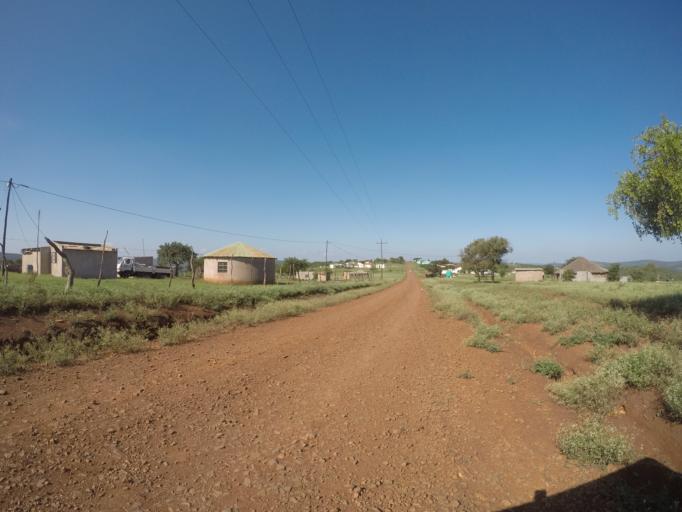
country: ZA
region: KwaZulu-Natal
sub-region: uThungulu District Municipality
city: Empangeni
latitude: -28.5724
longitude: 31.7284
